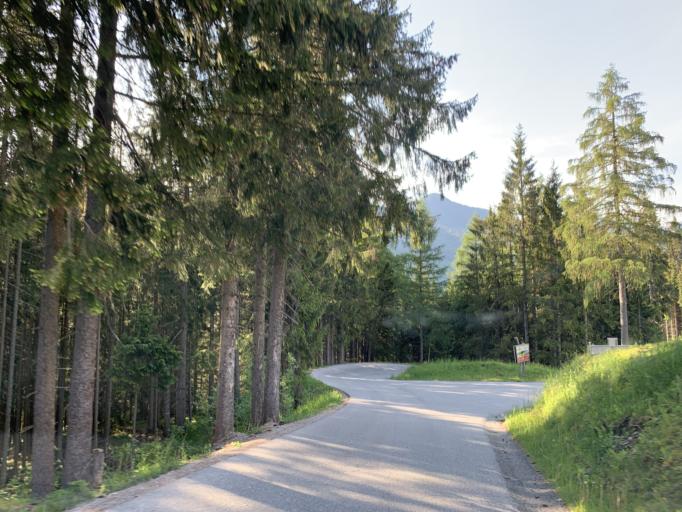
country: AT
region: Salzburg
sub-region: Politischer Bezirk Sankt Johann im Pongau
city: Forstau
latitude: 47.3767
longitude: 13.6084
